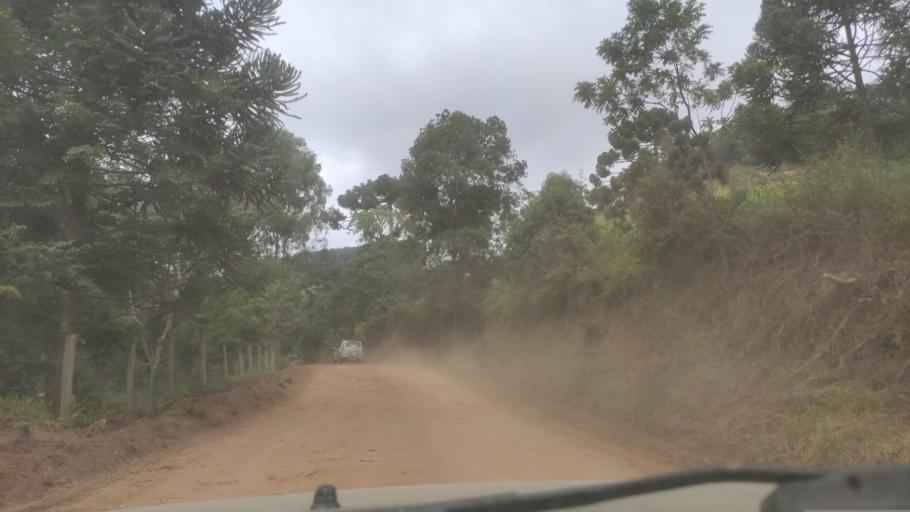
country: BR
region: Minas Gerais
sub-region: Cambui
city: Cambui
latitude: -22.6591
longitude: -45.9080
